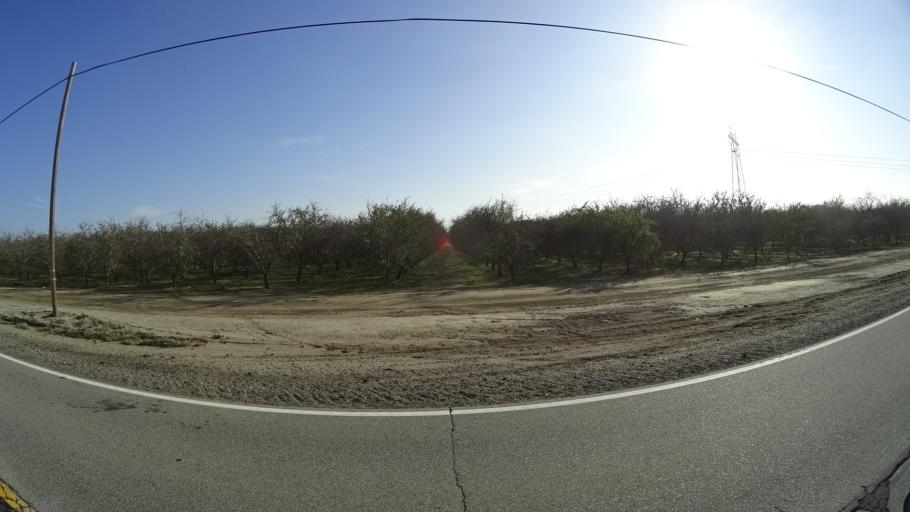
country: US
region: California
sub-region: Kern County
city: Rosedale
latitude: 35.2962
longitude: -119.1692
